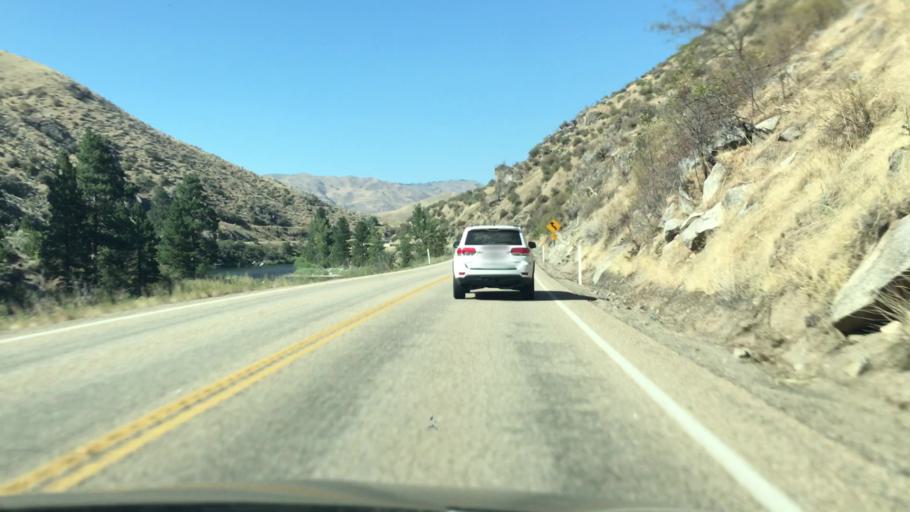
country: US
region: Idaho
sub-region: Ada County
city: Eagle
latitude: 43.9523
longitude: -116.1941
